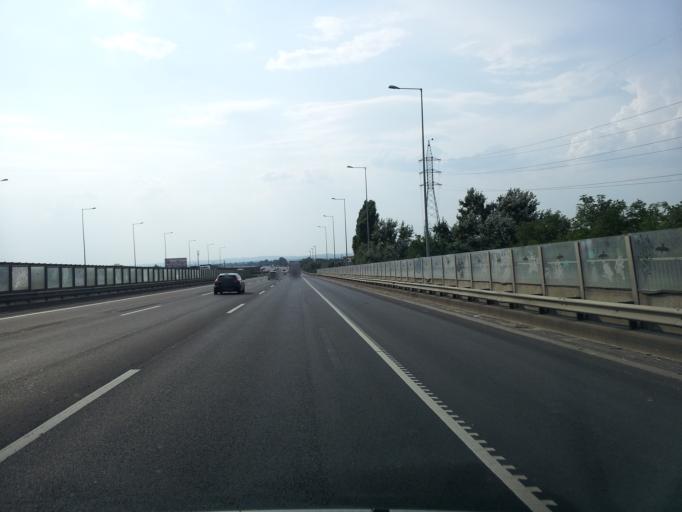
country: HU
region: Pest
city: Dunaharaszti
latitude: 47.3722
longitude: 19.0904
